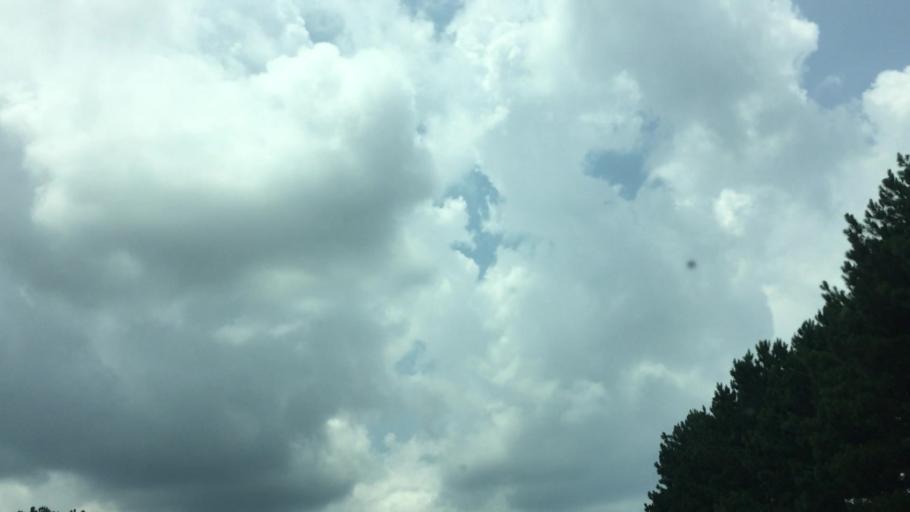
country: US
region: Georgia
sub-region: Fulton County
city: Fairburn
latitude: 33.6107
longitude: -84.6101
